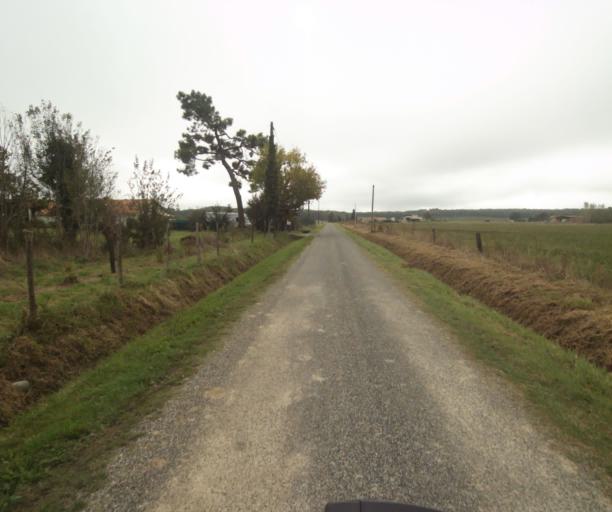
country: FR
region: Midi-Pyrenees
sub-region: Departement du Tarn-et-Garonne
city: Campsas
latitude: 43.8803
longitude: 1.3581
